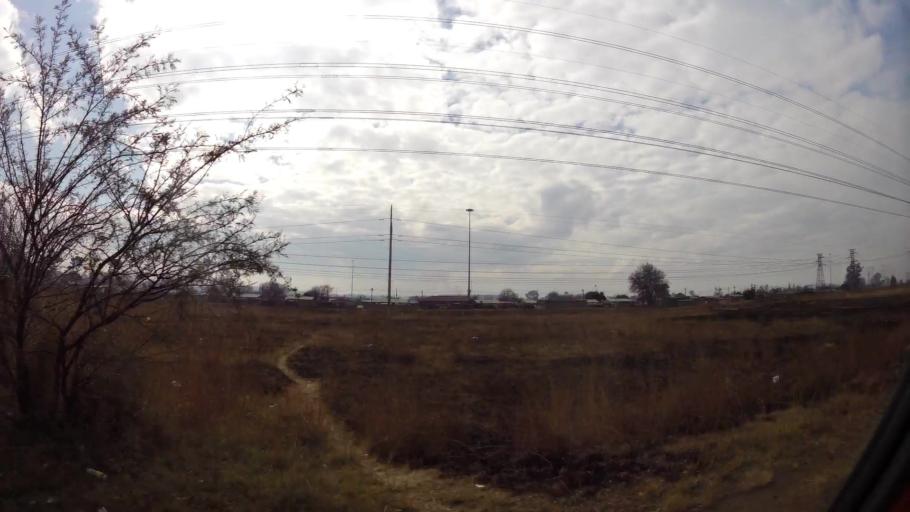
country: ZA
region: Gauteng
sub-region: Sedibeng District Municipality
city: Vanderbijlpark
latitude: -26.6785
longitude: 27.8453
